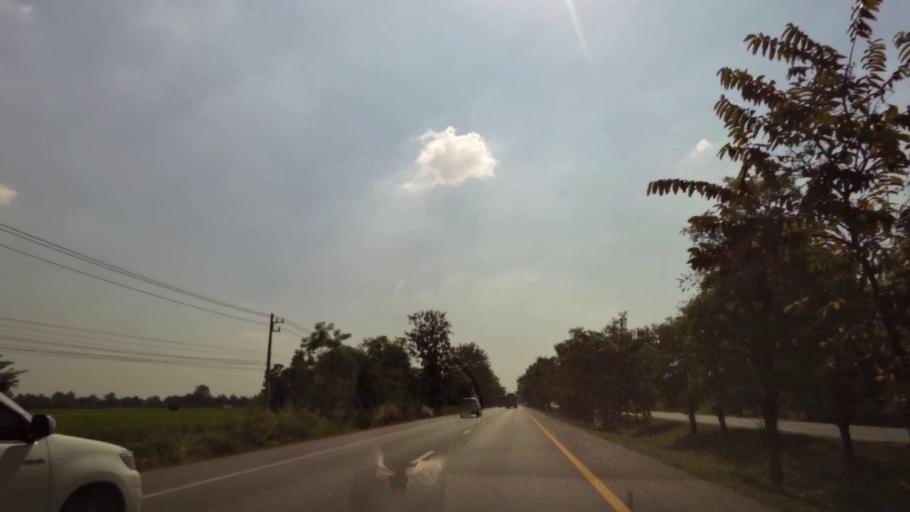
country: TH
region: Phichit
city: Bueng Na Rang
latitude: 16.1656
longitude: 100.1264
